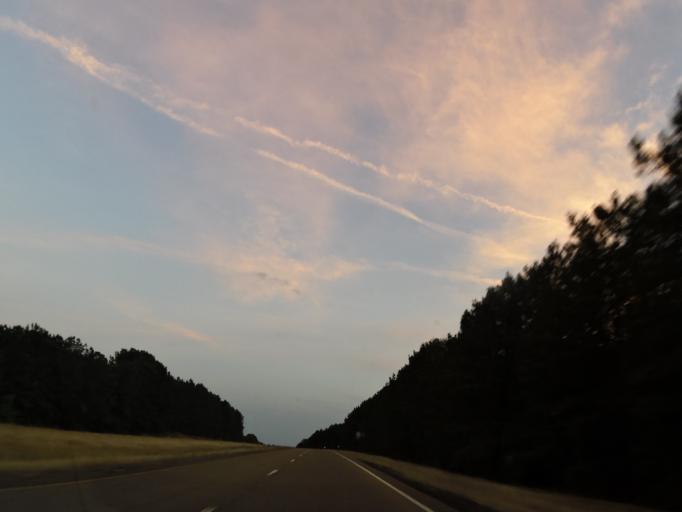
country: US
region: Mississippi
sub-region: Lauderdale County
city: Meridian Station
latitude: 32.6137
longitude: -88.4991
